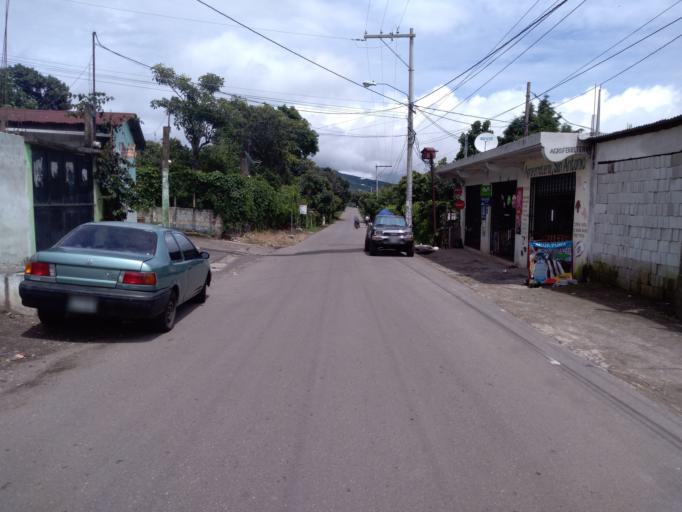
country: GT
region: Escuintla
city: San Vicente Pacaya
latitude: 14.3677
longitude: -90.5634
